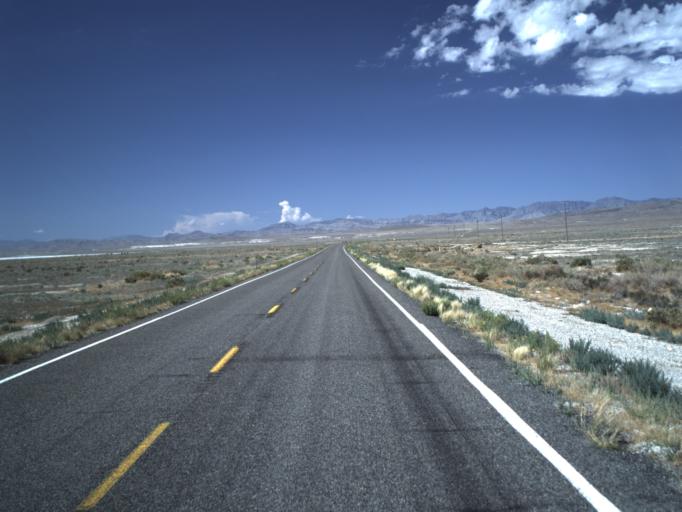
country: US
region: Utah
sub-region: Millard County
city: Delta
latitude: 39.0961
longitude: -113.1619
